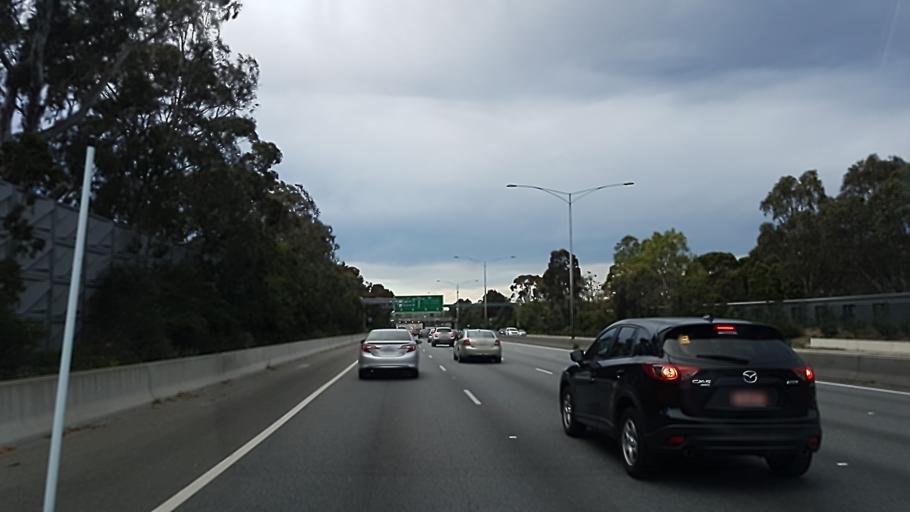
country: AU
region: Victoria
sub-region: Stonnington
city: Glen Iris
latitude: -37.8638
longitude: 145.0602
